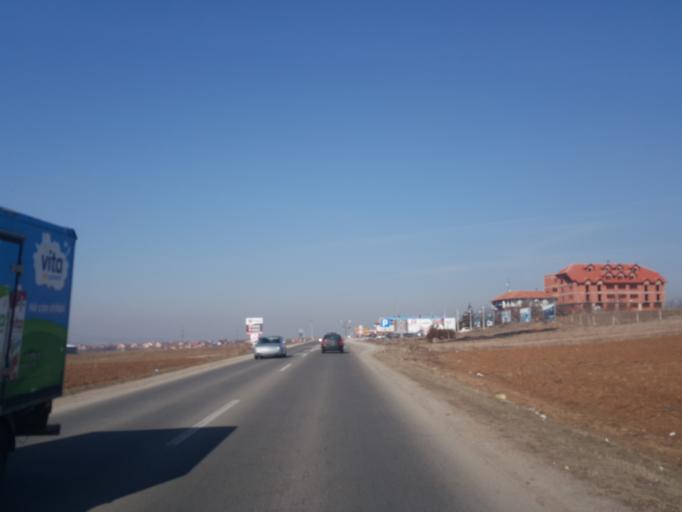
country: XK
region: Mitrovica
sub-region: Vushtrri
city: Vushtrri
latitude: 42.7730
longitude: 21.0184
